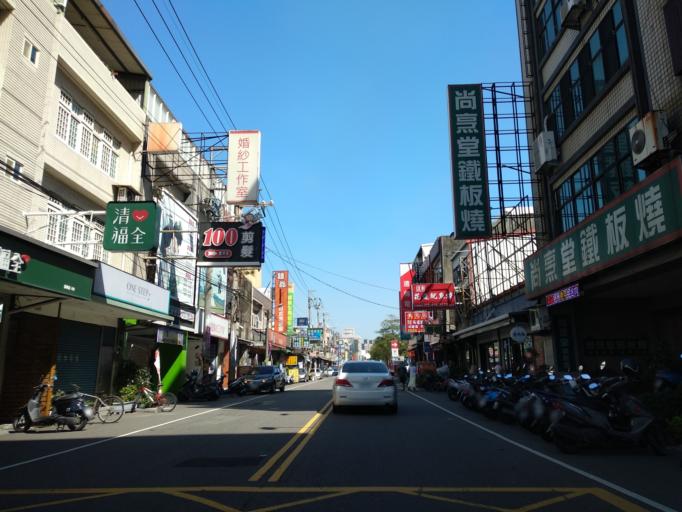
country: TW
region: Taiwan
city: Taoyuan City
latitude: 24.9547
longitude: 121.2333
